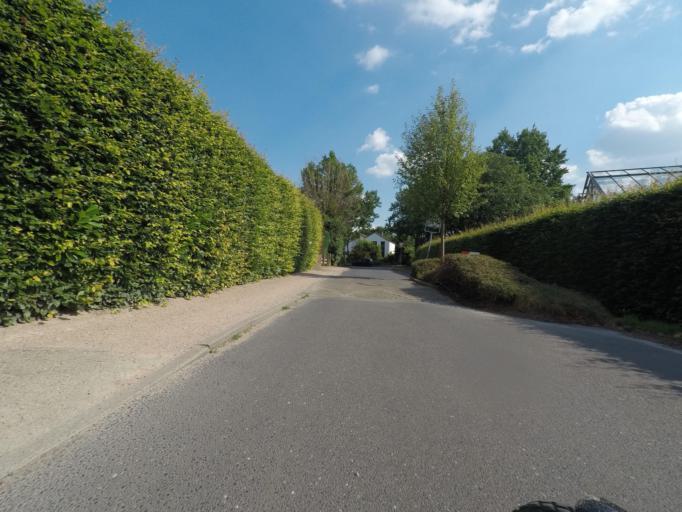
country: DE
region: Hamburg
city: Sasel
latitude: 53.6421
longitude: 10.1078
